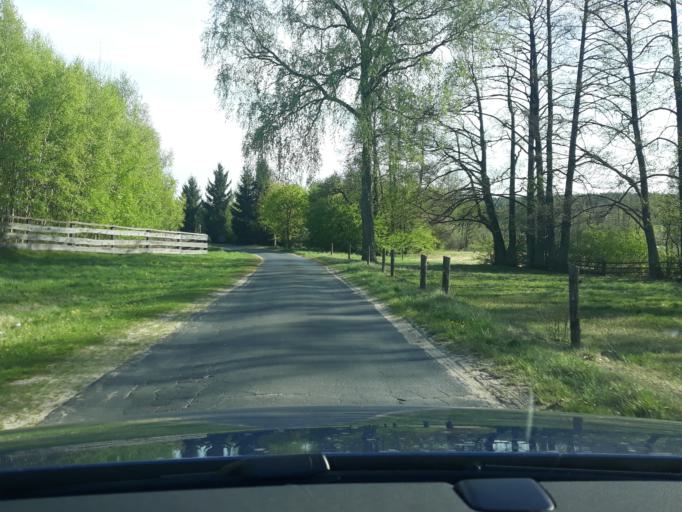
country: PL
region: Pomeranian Voivodeship
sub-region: Powiat czluchowski
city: Przechlewo
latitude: 53.8796
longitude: 17.3228
